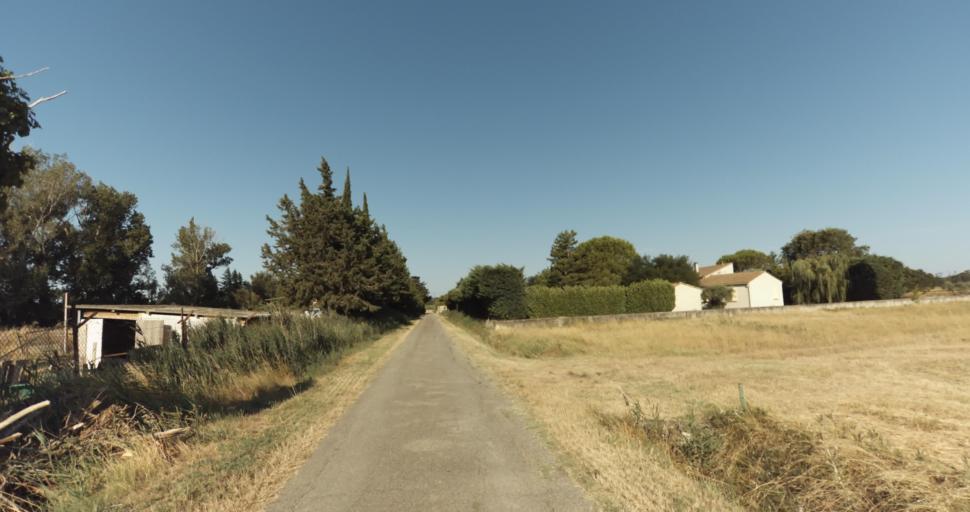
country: FR
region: Provence-Alpes-Cote d'Azur
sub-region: Departement du Vaucluse
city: Althen-des-Paluds
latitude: 44.0424
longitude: 4.9429
